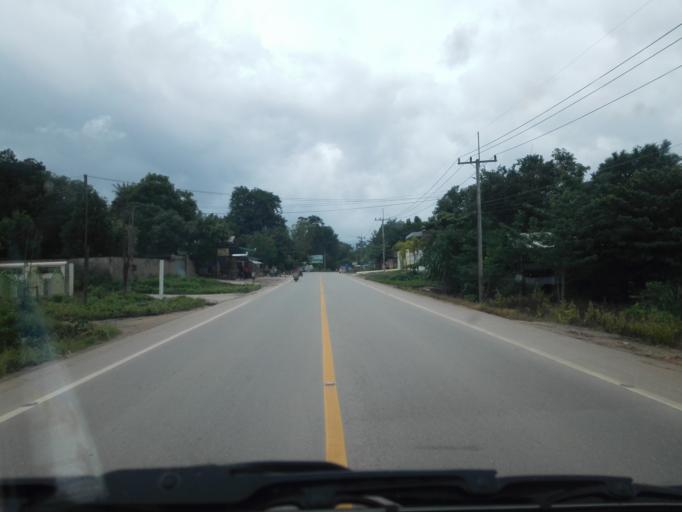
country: TH
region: Tak
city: Mae Sot
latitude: 16.6893
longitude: 98.4409
